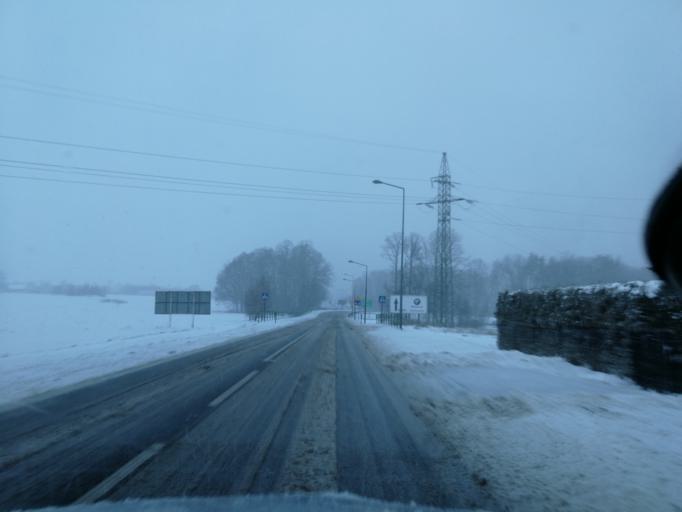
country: PL
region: Silesian Voivodeship
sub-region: Powiat pszczynski
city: Radostowice
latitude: 49.9968
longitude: 18.8958
